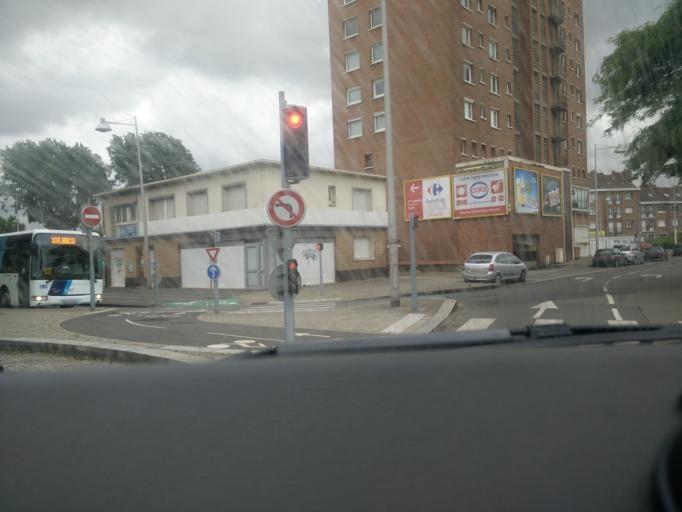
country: FR
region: Nord-Pas-de-Calais
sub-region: Departement du Nord
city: Dunkerque
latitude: 51.0327
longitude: 2.3716
